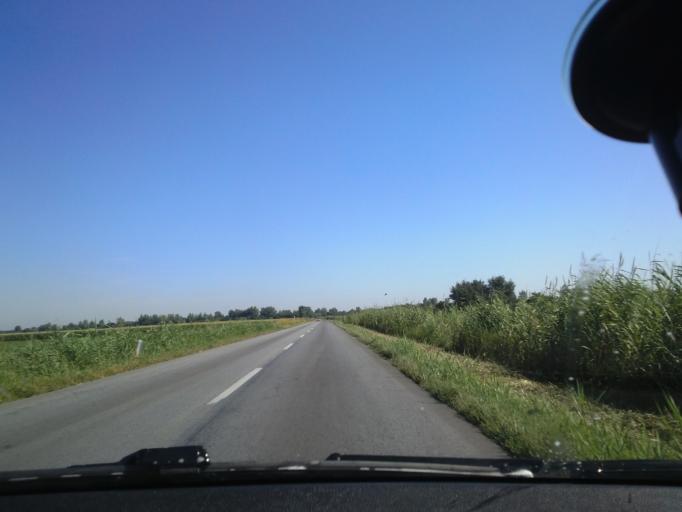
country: RS
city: Rumenka
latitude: 45.3025
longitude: 19.7275
